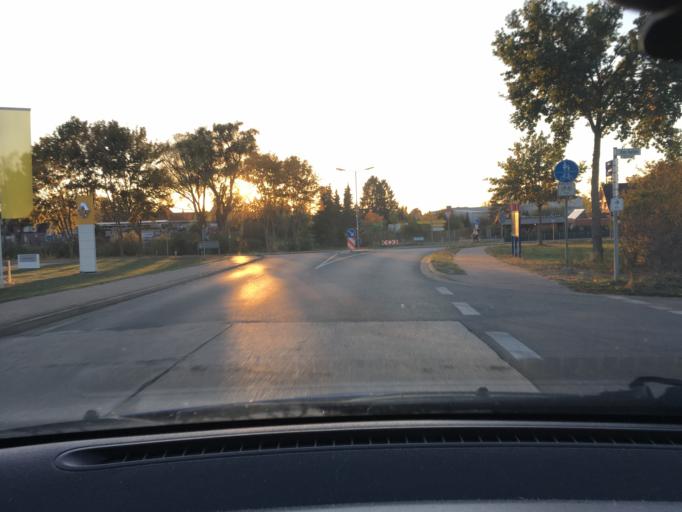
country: DE
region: Lower Saxony
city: Bleckede
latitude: 53.2847
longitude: 10.7416
